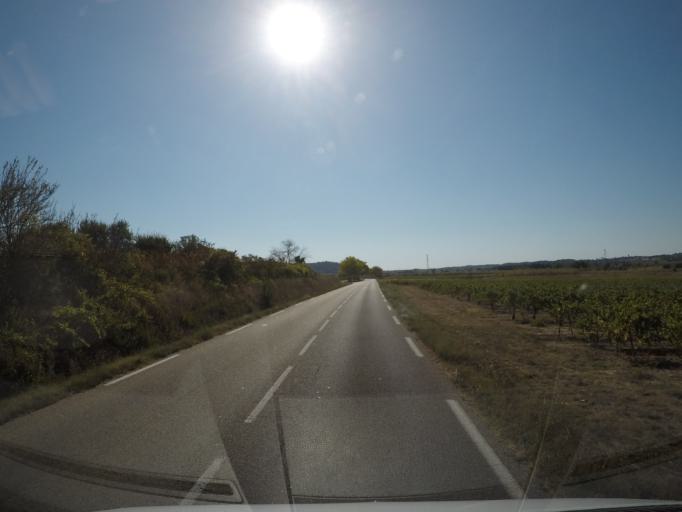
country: FR
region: Languedoc-Roussillon
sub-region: Departement du Gard
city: Ledignan
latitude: 44.0136
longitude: 4.1102
